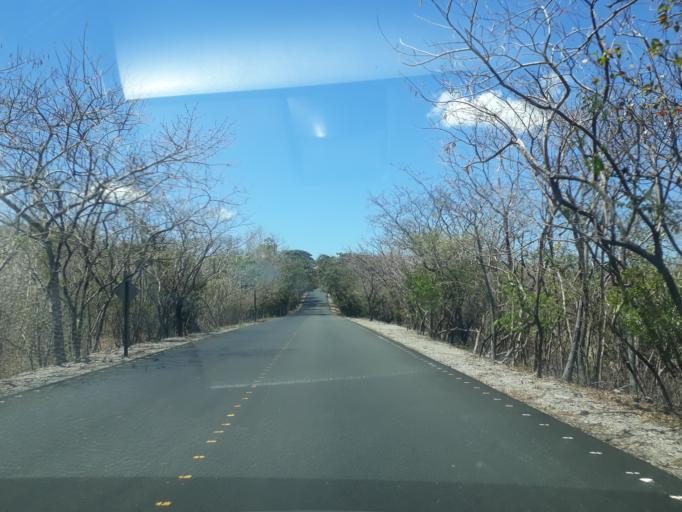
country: CR
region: Guanacaste
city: La Cruz
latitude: 10.8780
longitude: -85.5869
